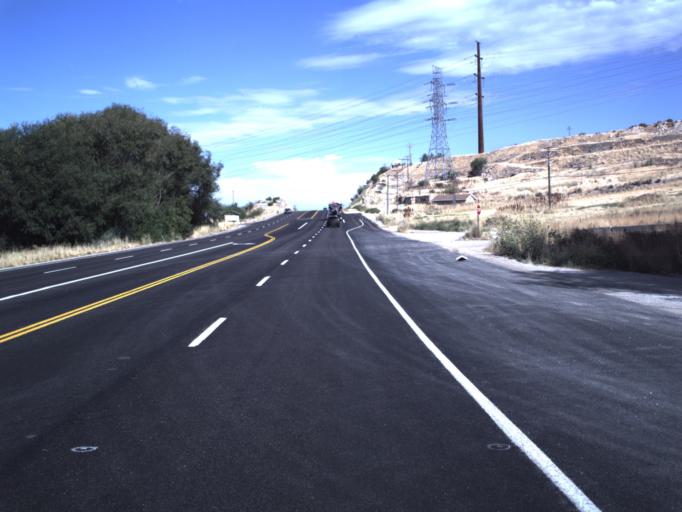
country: US
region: Utah
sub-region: Box Elder County
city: South Willard
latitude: 41.3343
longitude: -112.0265
